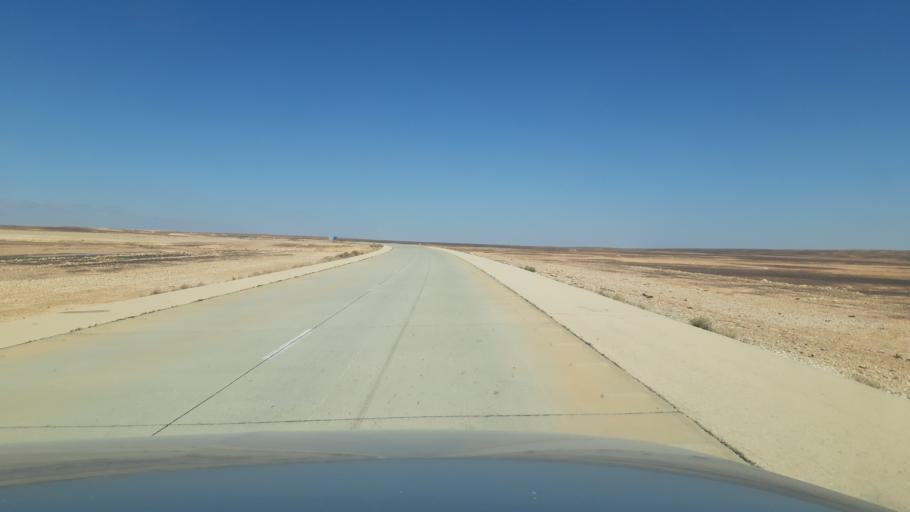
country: SA
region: Al Jawf
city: Al Qurayyat
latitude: 31.1071
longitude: 36.6435
